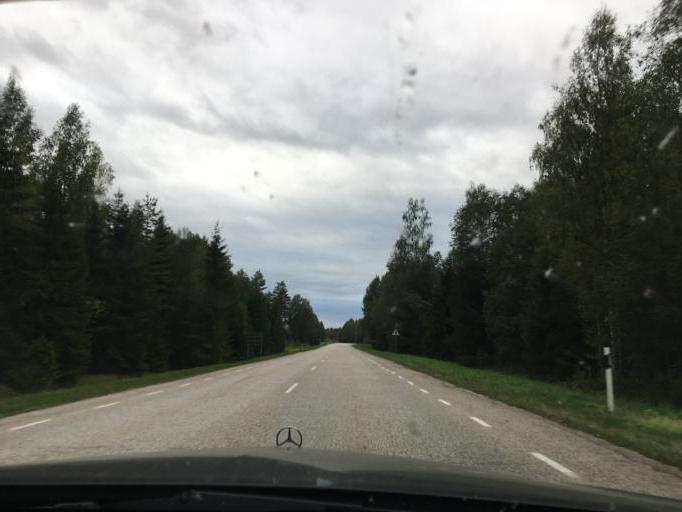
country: LV
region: Aluksnes Rajons
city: Aluksne
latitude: 57.6286
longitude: 27.3002
